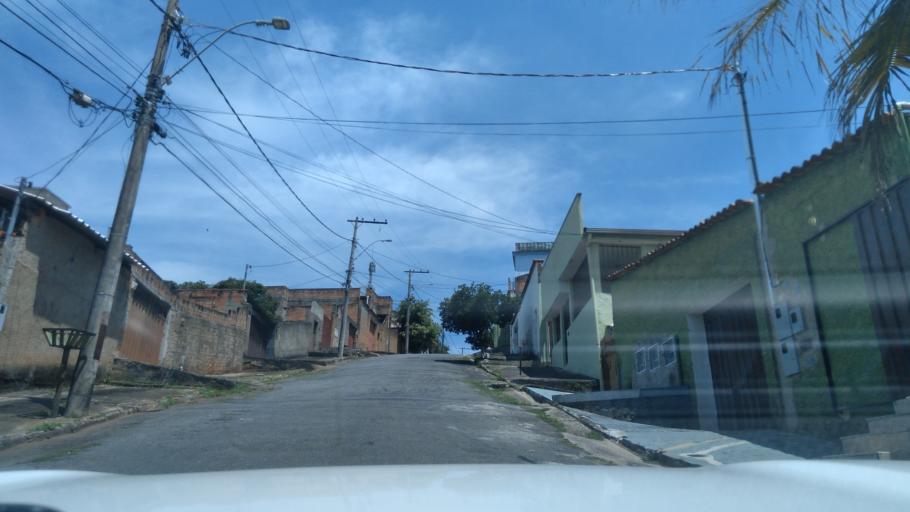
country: BR
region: Minas Gerais
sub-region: Contagem
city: Contagem
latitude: -19.9078
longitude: -44.0143
